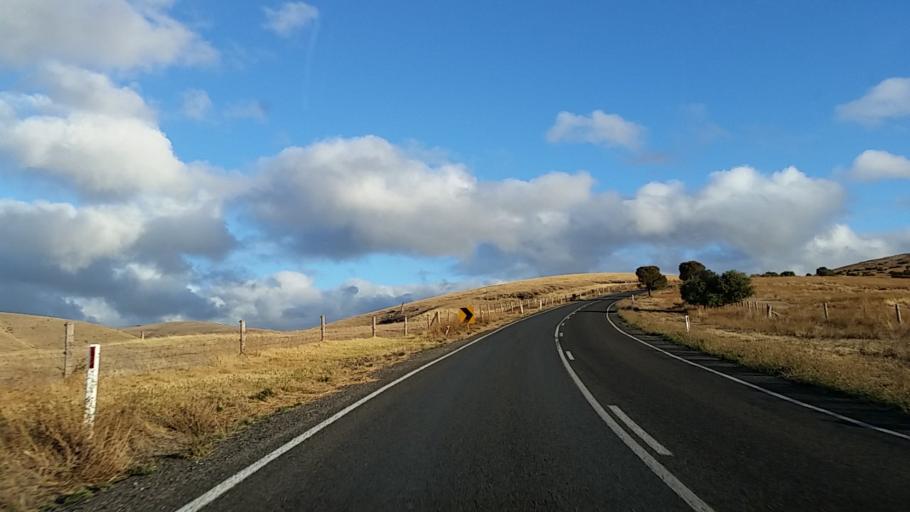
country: AU
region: South Australia
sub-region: Yankalilla
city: Normanville
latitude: -35.5336
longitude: 138.1941
